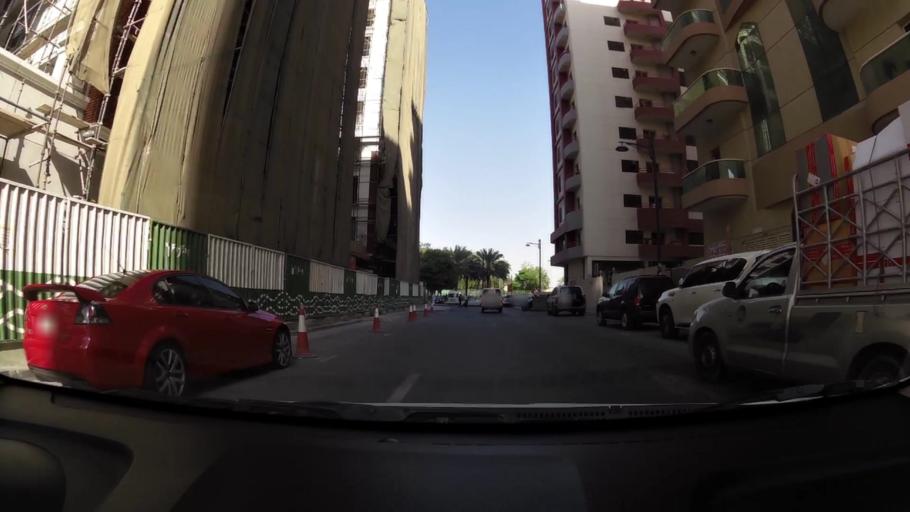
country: AE
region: Ash Shariqah
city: Sharjah
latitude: 25.2921
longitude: 55.3805
